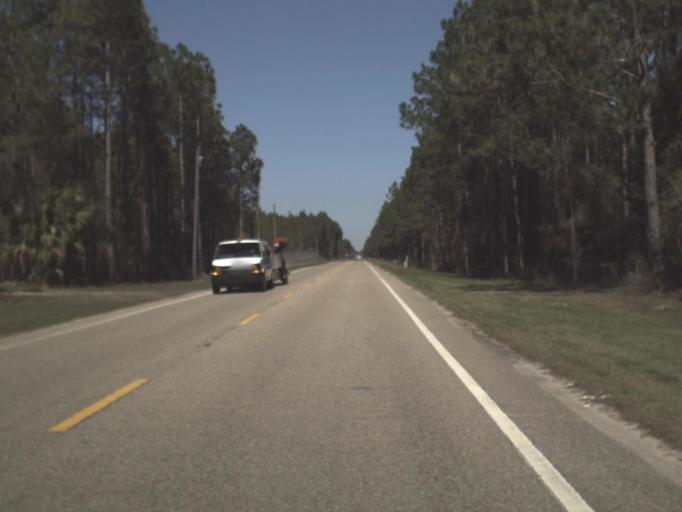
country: US
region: Florida
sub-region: Gulf County
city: Port Saint Joe
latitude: 29.8496
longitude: -85.2584
